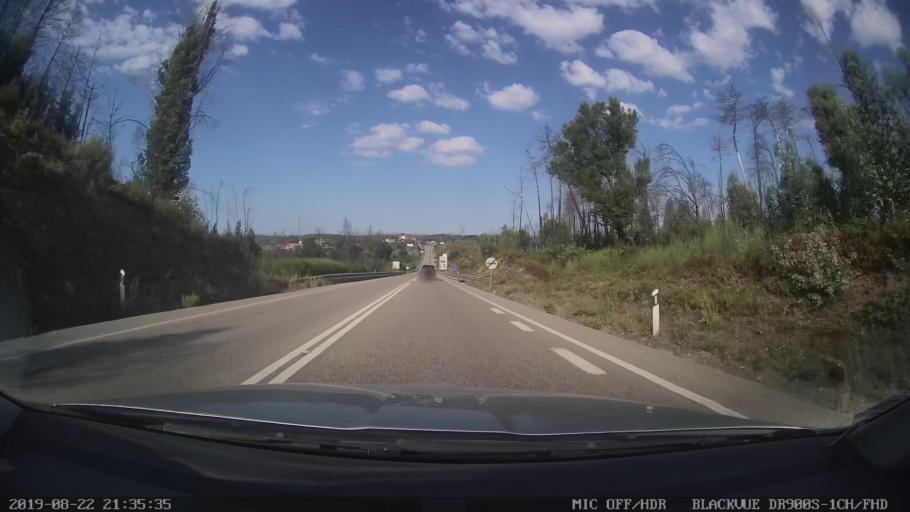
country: PT
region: Leiria
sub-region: Pedrogao Grande
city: Pedrogao Grande
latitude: 39.9240
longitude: -8.2094
